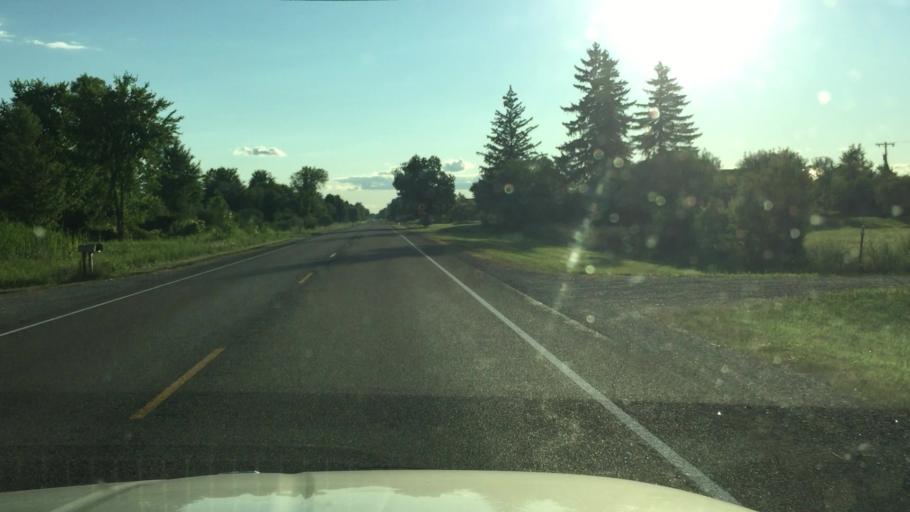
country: US
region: Michigan
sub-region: Saint Clair County
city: Capac
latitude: 43.0265
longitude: -82.9646
